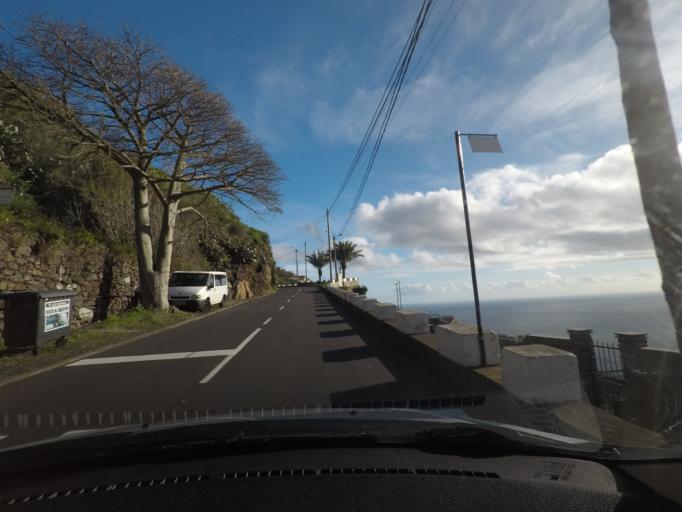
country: PT
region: Madeira
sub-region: Ribeira Brava
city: Campanario
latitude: 32.6704
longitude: -17.0386
